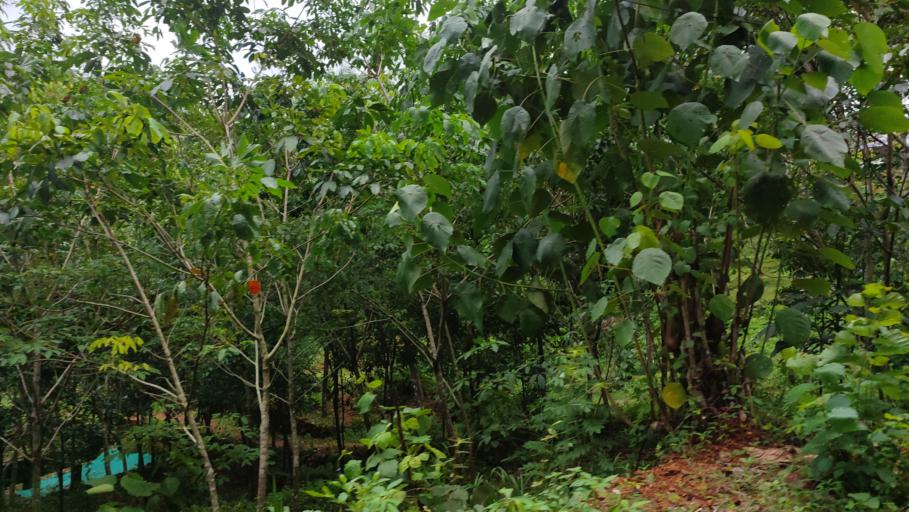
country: IN
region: Kerala
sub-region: Kasaragod District
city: Nileshwar
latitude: 12.2994
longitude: 75.2963
